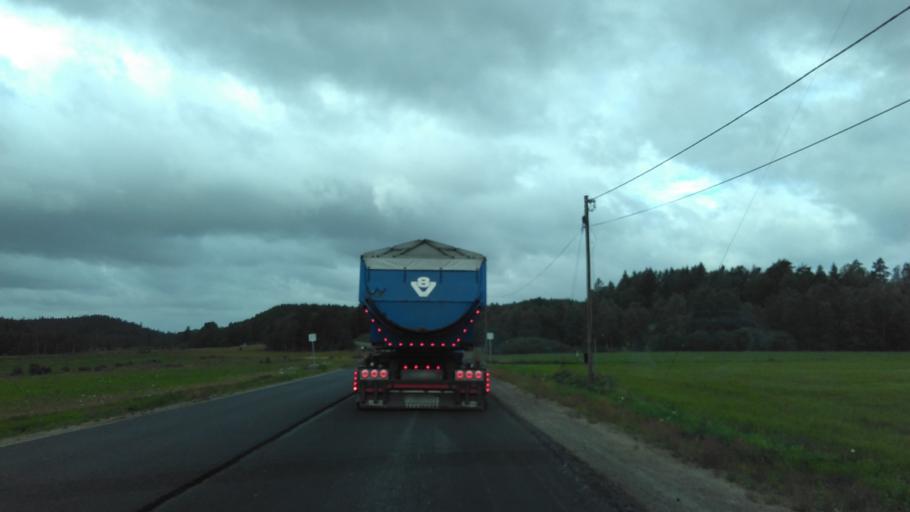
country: SE
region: Vaestra Goetaland
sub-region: Marks Kommun
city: Fritsla
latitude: 57.5688
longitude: 12.8251
